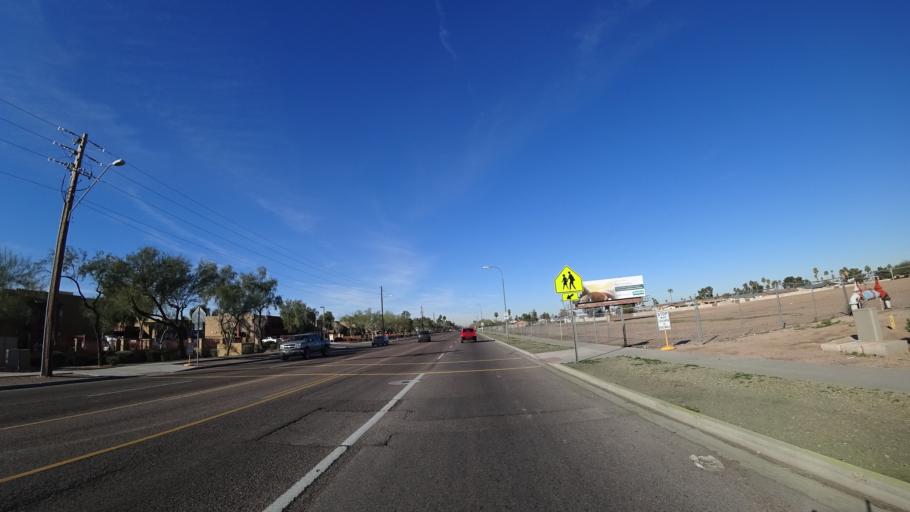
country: US
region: Arizona
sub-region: Maricopa County
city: Tolleson
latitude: 33.4659
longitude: -112.2060
